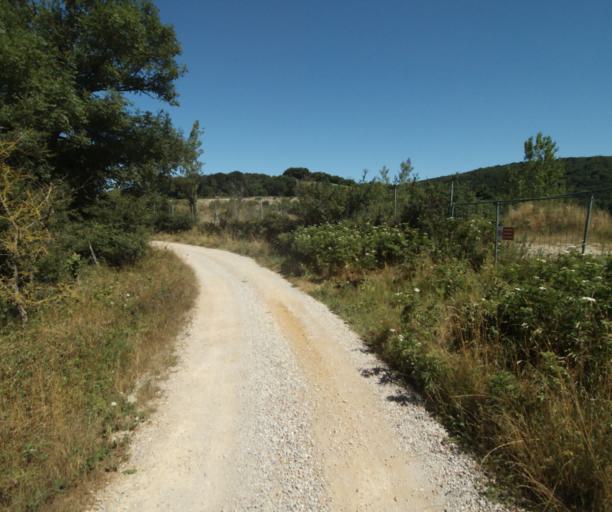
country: FR
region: Midi-Pyrenees
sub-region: Departement du Tarn
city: Soreze
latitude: 43.4429
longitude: 2.0914
